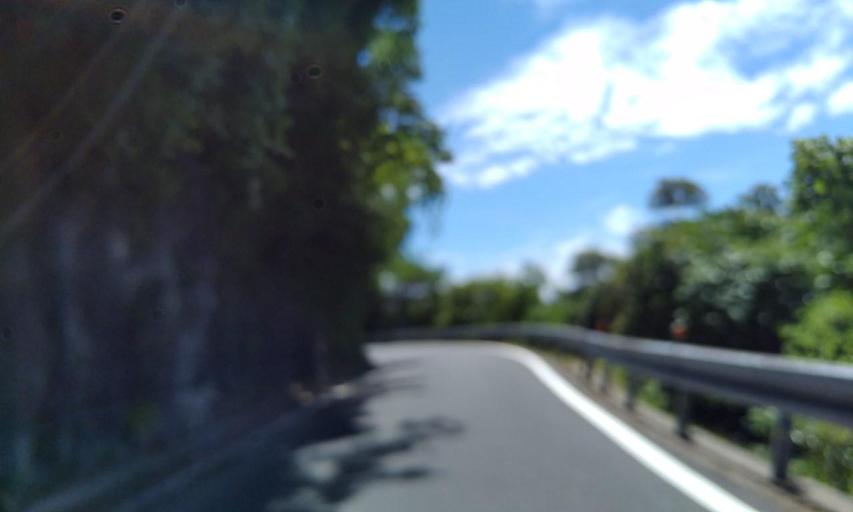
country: JP
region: Kyoto
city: Miyazu
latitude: 35.6667
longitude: 135.2718
